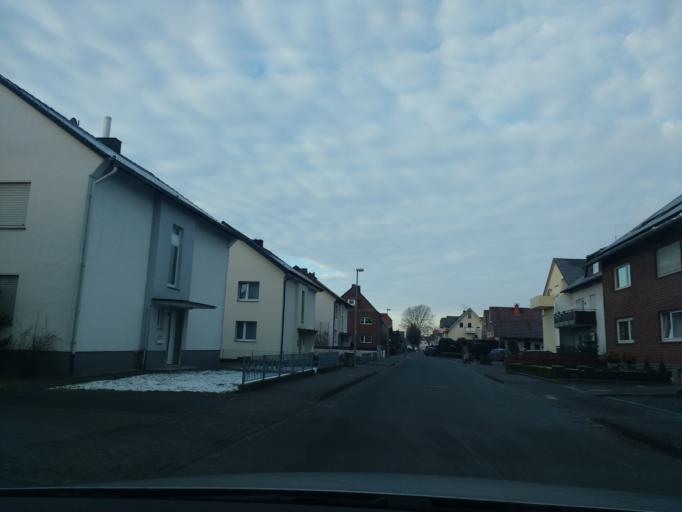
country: DE
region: North Rhine-Westphalia
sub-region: Regierungsbezirk Detmold
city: Paderborn
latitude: 51.7291
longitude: 8.6882
